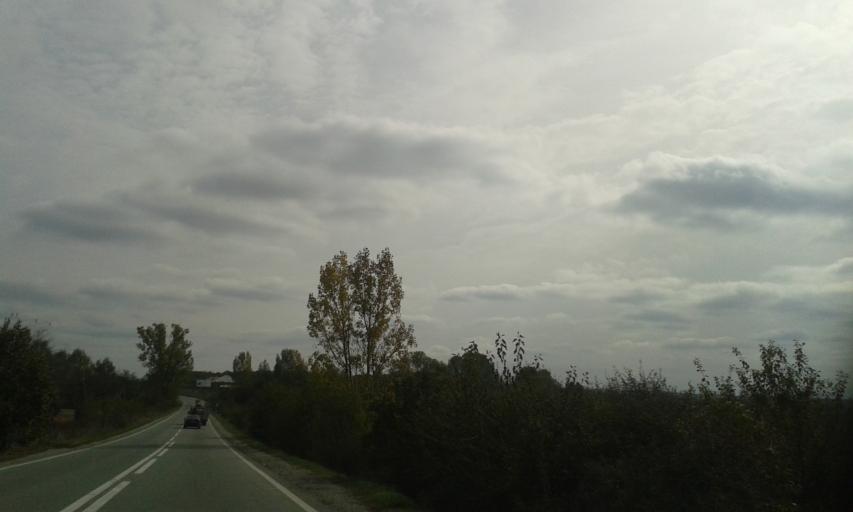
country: RO
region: Gorj
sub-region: Comuna Scoarta
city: Scoarta
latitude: 45.0257
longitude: 23.4368
